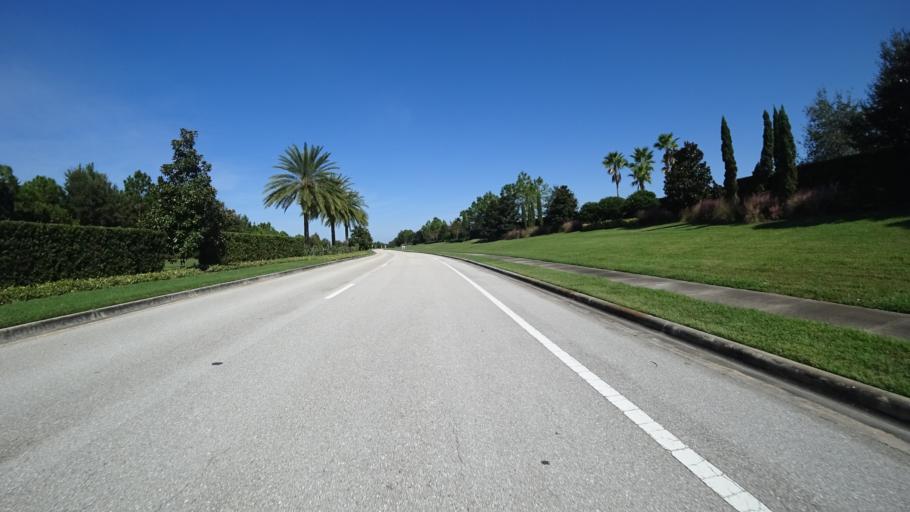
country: US
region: Florida
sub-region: Sarasota County
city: The Meadows
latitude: 27.3986
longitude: -82.3853
